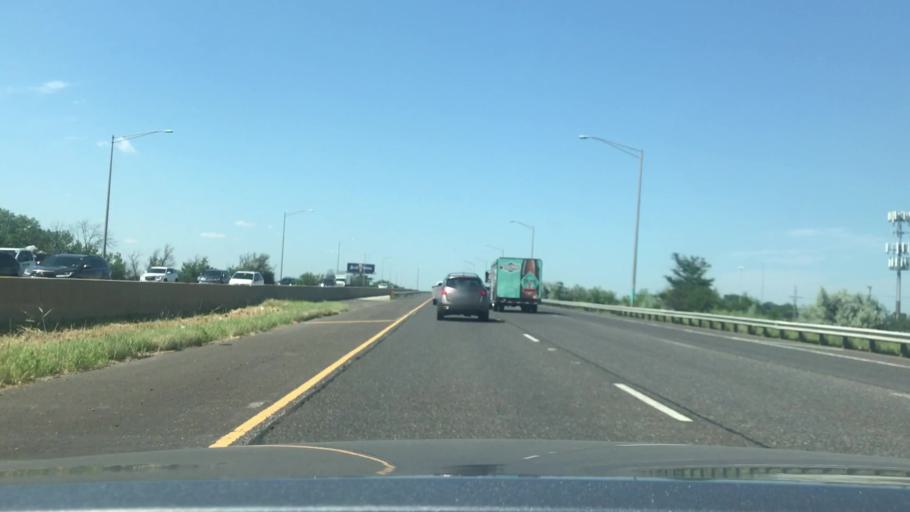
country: US
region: Illinois
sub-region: Cook County
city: Dixmoor
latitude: 41.6449
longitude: -87.6611
